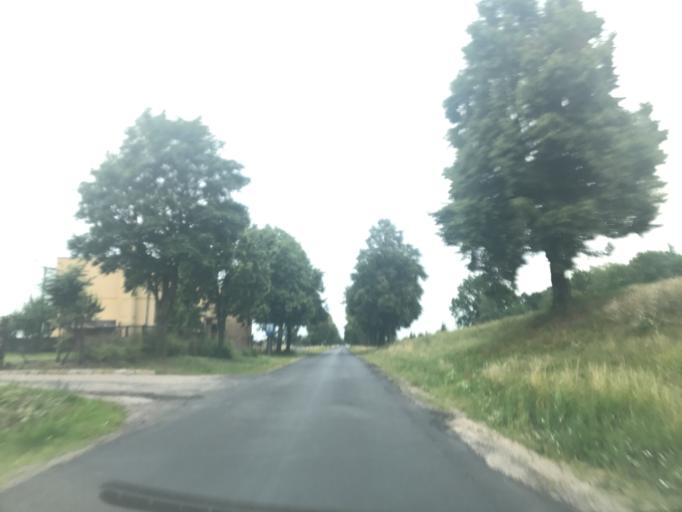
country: PL
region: Kujawsko-Pomorskie
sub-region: Powiat lipnowski
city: Lipno
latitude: 52.8213
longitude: 19.1837
